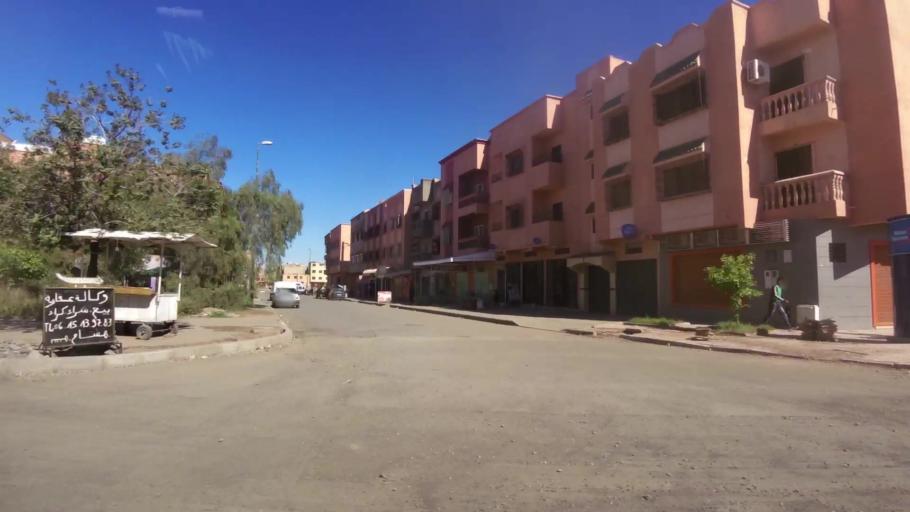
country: MA
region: Marrakech-Tensift-Al Haouz
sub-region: Marrakech
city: Marrakesh
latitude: 31.5952
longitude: -8.0504
